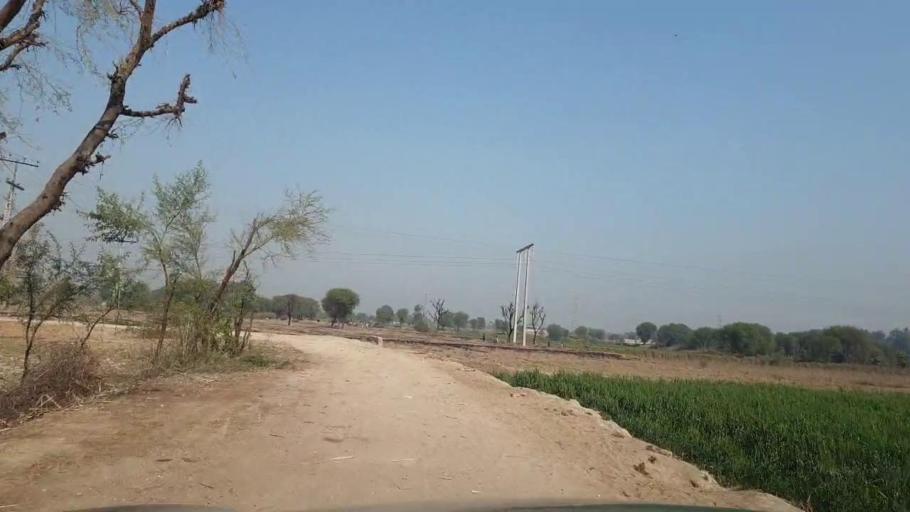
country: PK
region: Sindh
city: Tando Allahyar
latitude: 25.4675
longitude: 68.6991
